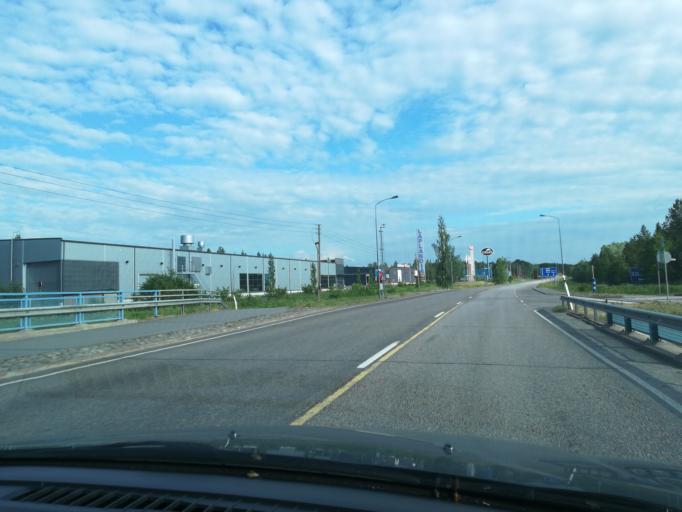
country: FI
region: South Karelia
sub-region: Imatra
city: Imatra
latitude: 61.1517
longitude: 28.8077
